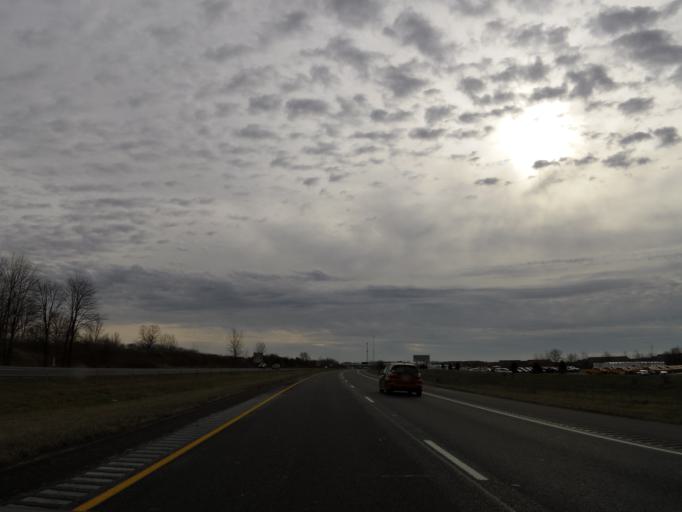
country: US
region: Indiana
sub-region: Hendricks County
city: Brownsburg
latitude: 39.8563
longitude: -86.3811
